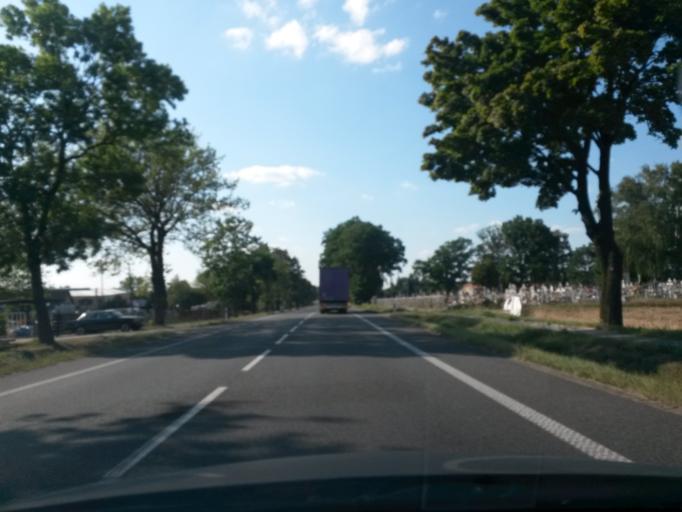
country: PL
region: Masovian Voivodeship
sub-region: Powiat sierpecki
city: Sierpc
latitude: 52.8472
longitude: 19.7114
